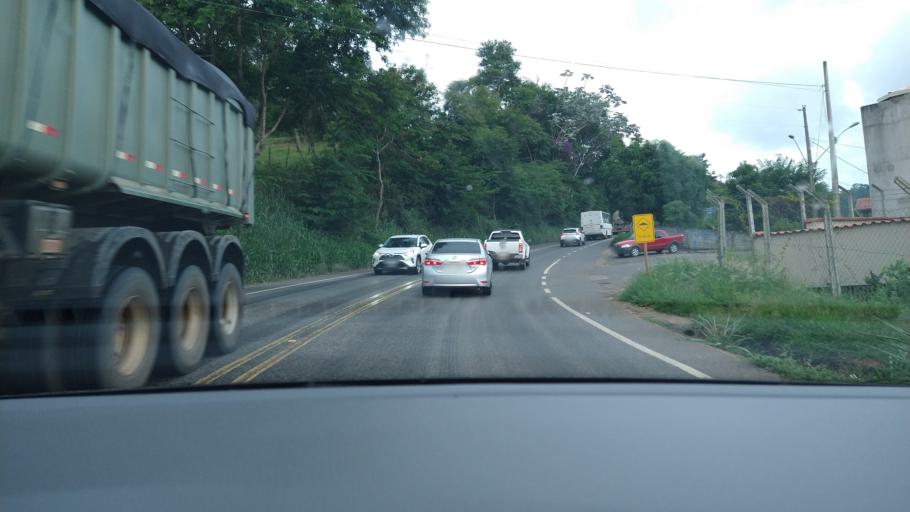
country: BR
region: Minas Gerais
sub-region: Vicosa
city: Vicosa
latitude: -20.6551
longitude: -42.8613
